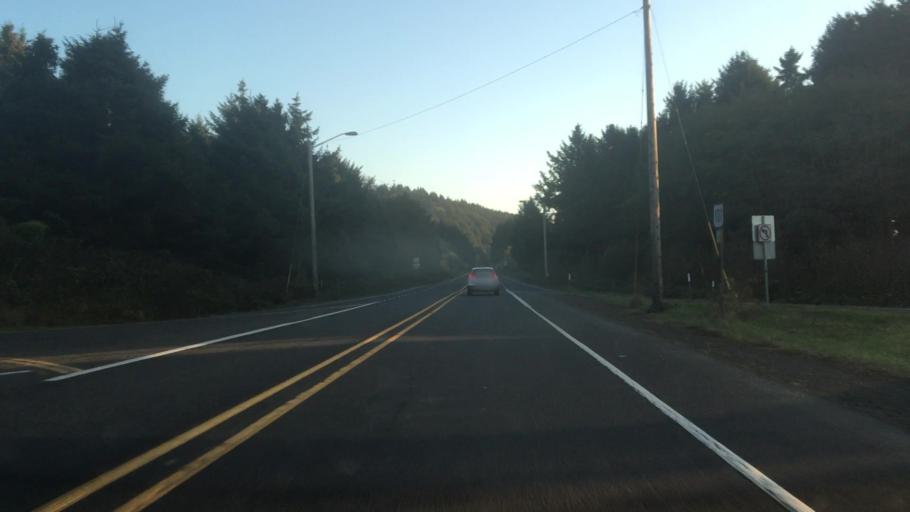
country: US
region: Oregon
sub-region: Clatsop County
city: Cannon Beach
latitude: 45.8713
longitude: -123.9583
